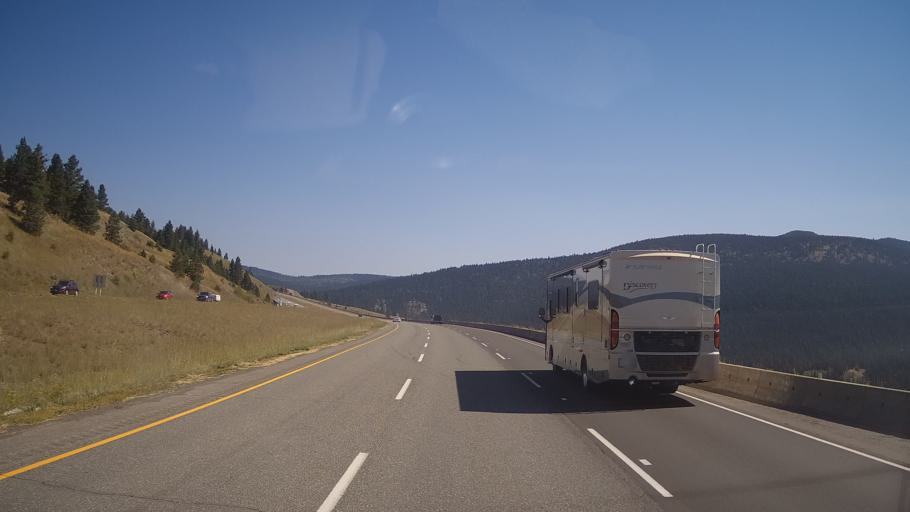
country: CA
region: British Columbia
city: Merritt
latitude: 50.1981
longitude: -120.6632
